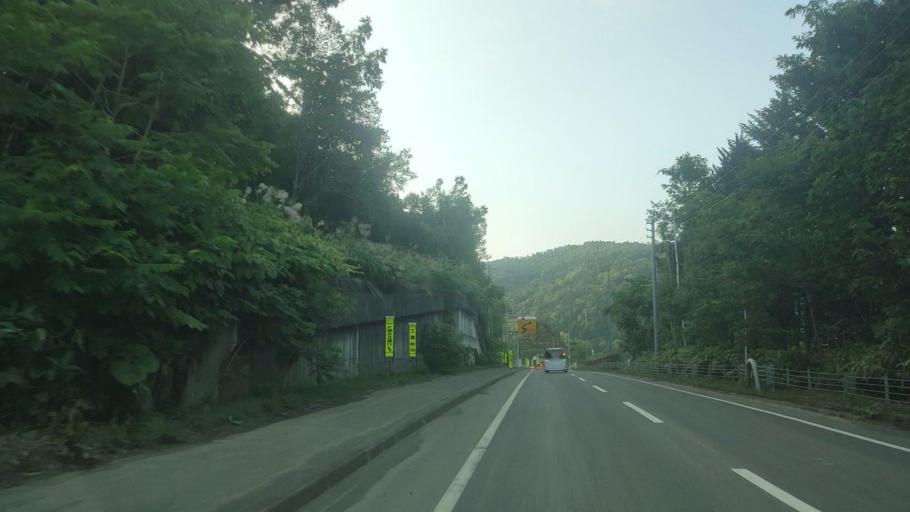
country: JP
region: Hokkaido
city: Bibai
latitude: 43.2308
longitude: 142.0397
